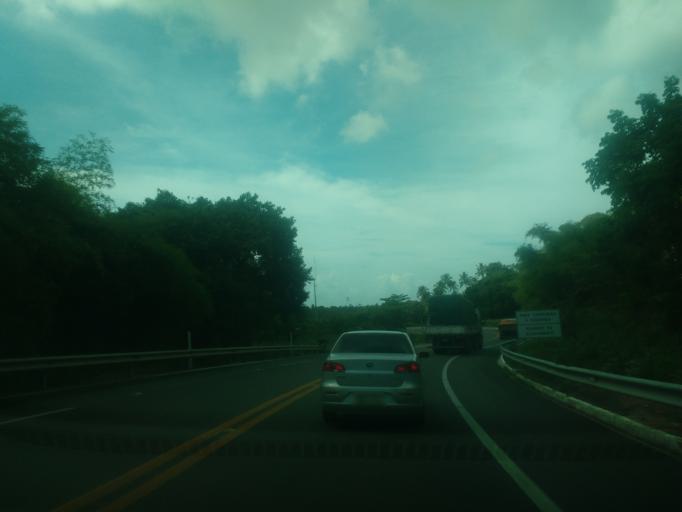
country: BR
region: Alagoas
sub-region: Marechal Deodoro
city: Marechal Deodoro
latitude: -9.6918
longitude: -35.8162
